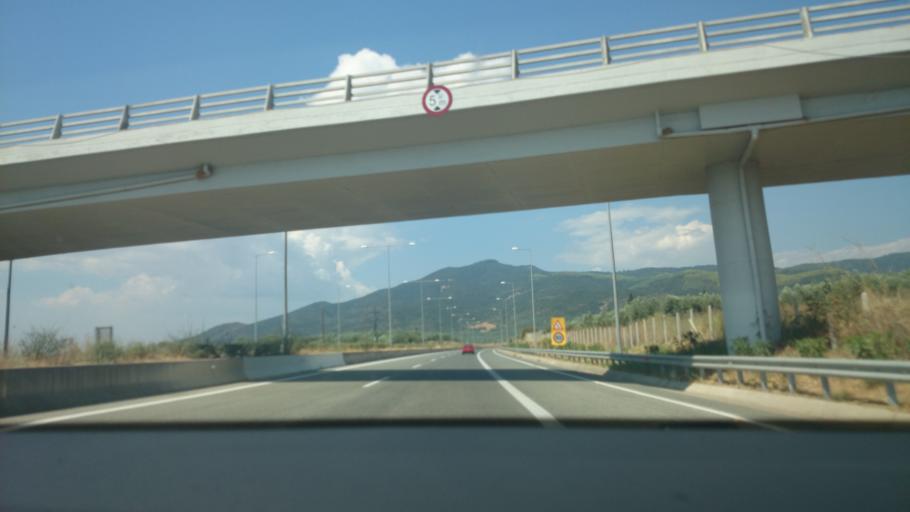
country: GR
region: West Greece
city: Aitoliko
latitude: 38.4856
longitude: 21.3454
